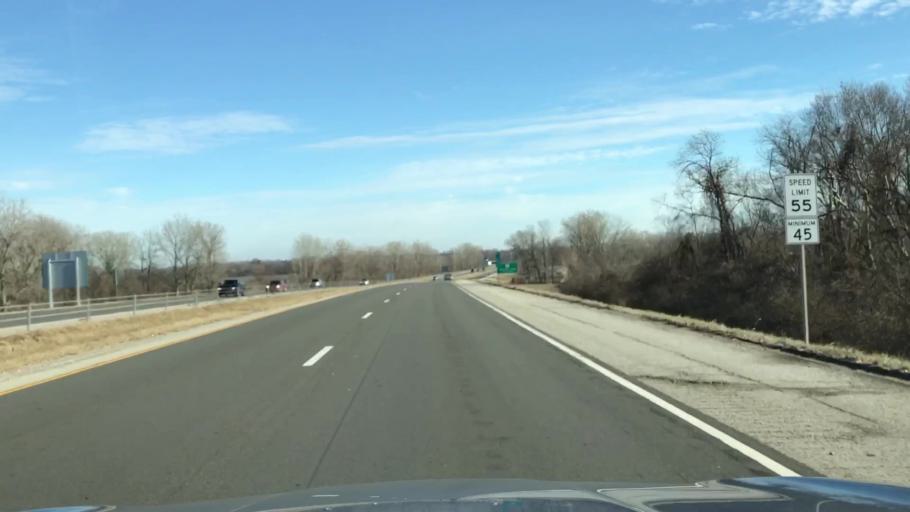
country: US
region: Illinois
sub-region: Madison County
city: Mitchell
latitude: 38.7656
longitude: -90.1138
